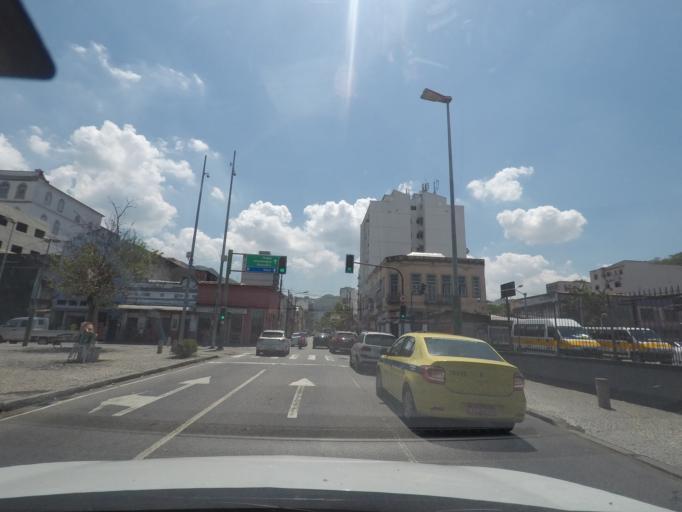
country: BR
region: Rio de Janeiro
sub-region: Rio De Janeiro
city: Rio de Janeiro
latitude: -22.9161
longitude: -43.2512
